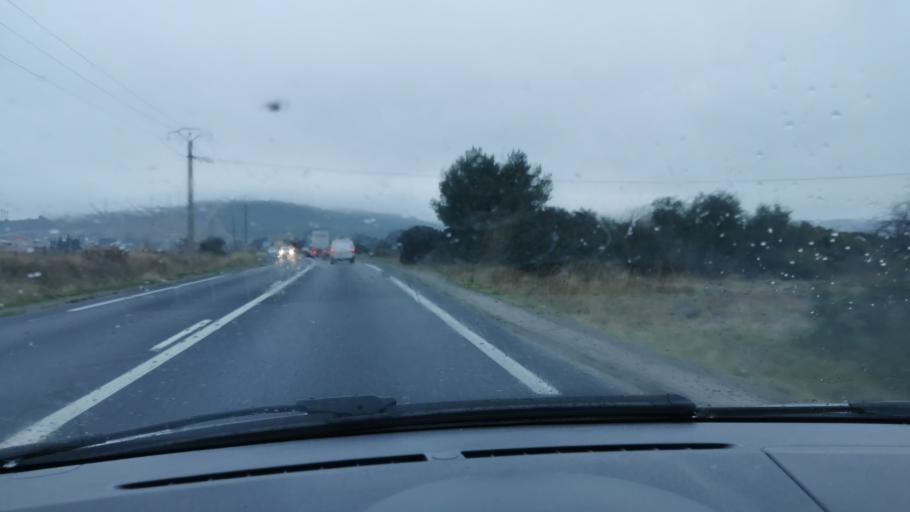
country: FR
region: Languedoc-Roussillon
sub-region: Departement de l'Herault
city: Frontignan
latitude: 43.4401
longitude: 3.7173
